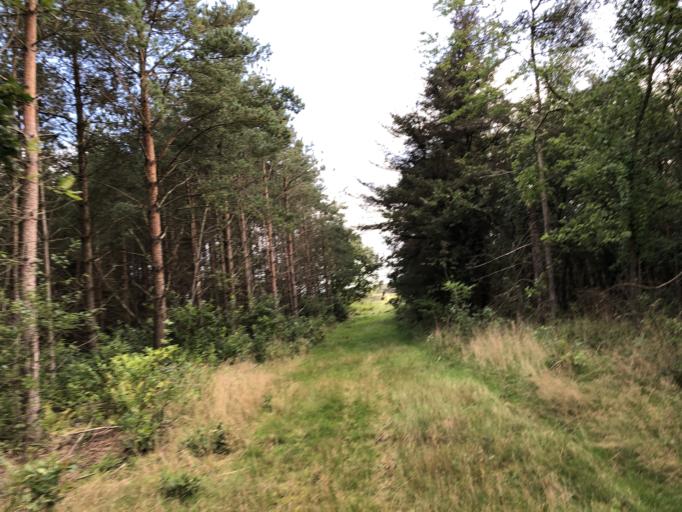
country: DK
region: Central Jutland
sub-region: Holstebro Kommune
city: Ulfborg
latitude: 56.3736
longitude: 8.3431
